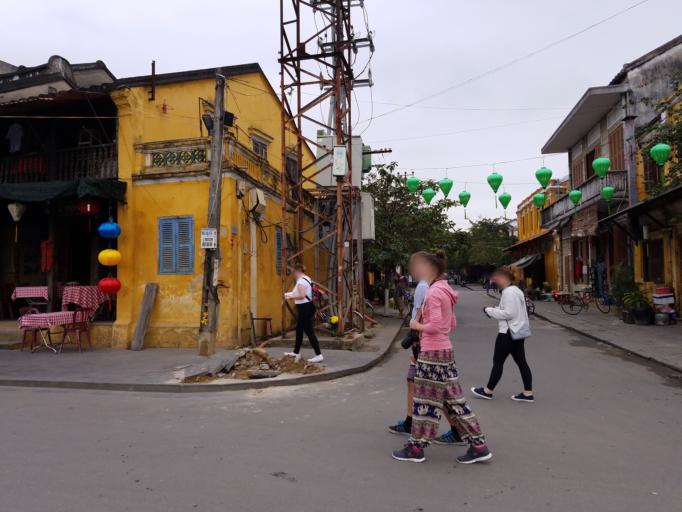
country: VN
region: Quang Nam
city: Hoi An
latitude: 15.8761
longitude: 108.3286
